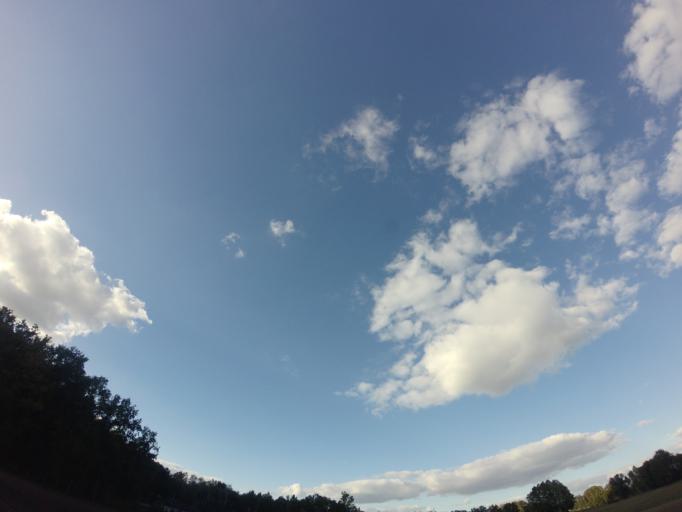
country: PL
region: Greater Poland Voivodeship
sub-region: Powiat nowotomyski
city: Nowy Tomysl
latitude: 52.2772
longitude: 16.1262
